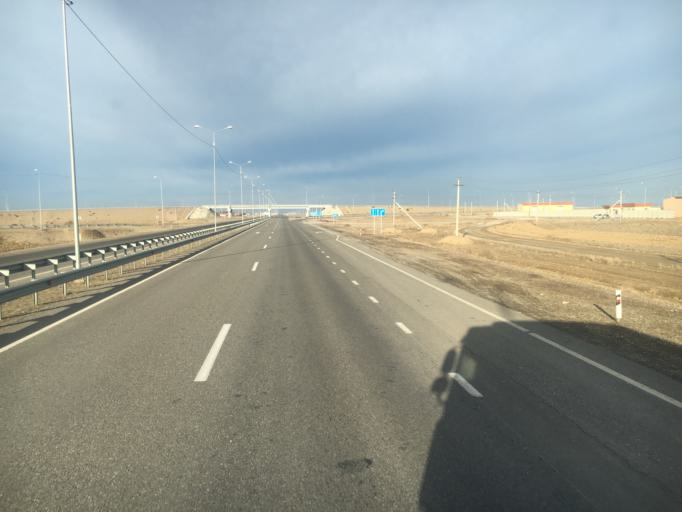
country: KZ
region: Ongtustik Qazaqstan
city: Turkestan
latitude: 43.4129
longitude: 68.0292
